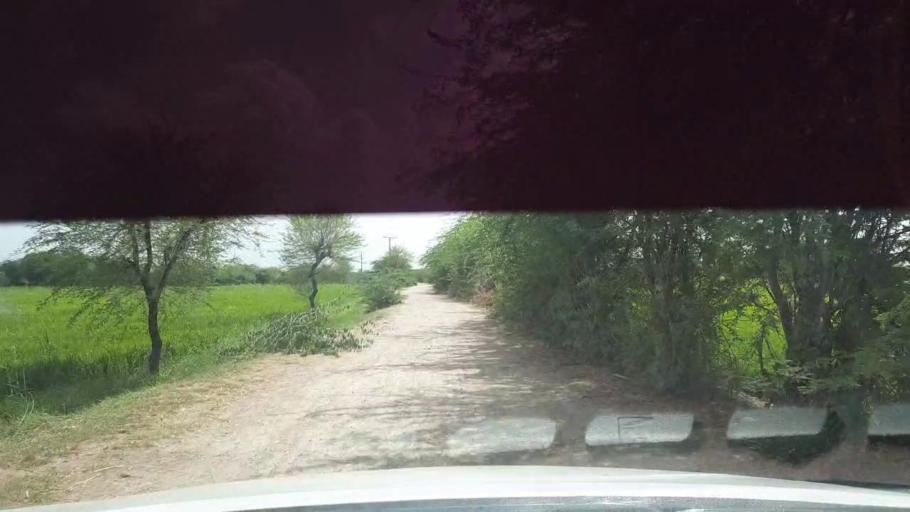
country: PK
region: Sindh
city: Kadhan
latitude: 24.6233
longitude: 69.0339
